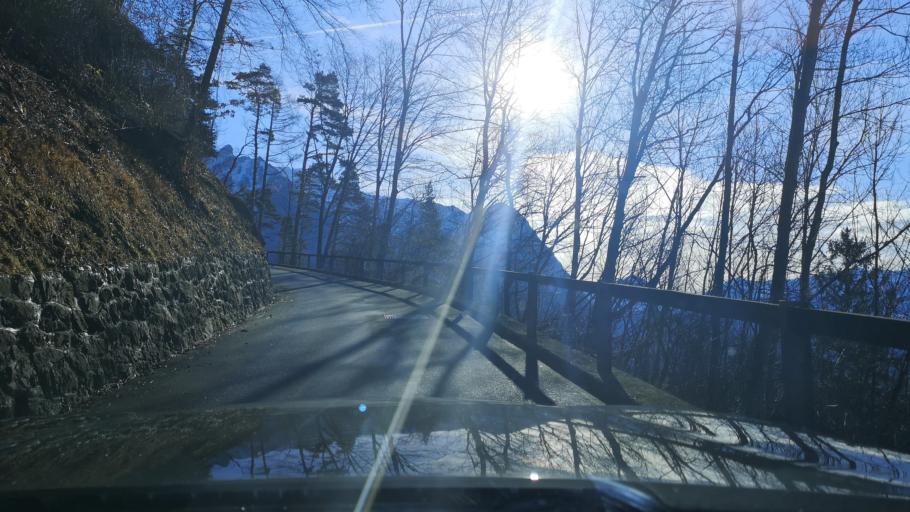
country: LI
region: Triesenberg
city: Triesenberg
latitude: 47.1223
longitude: 9.5359
